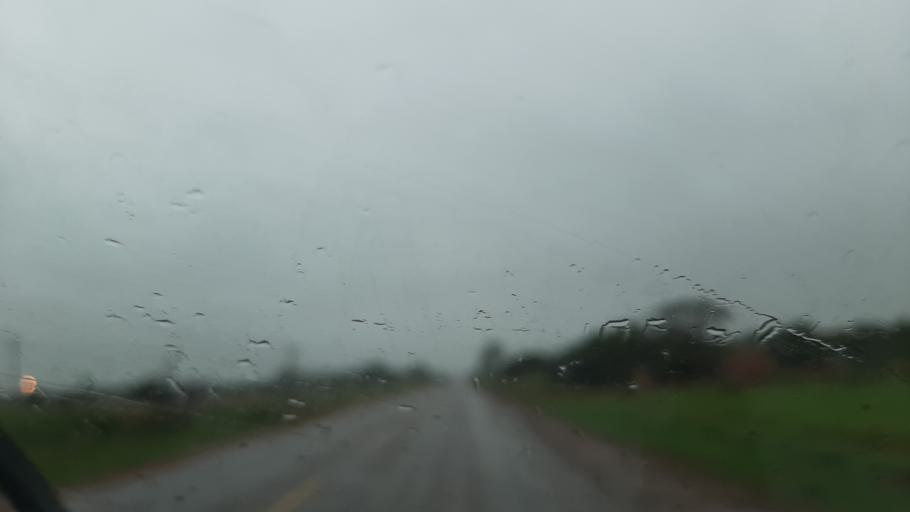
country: BO
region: Santa Cruz
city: Okinawa Numero Uno
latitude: -16.8598
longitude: -62.6106
